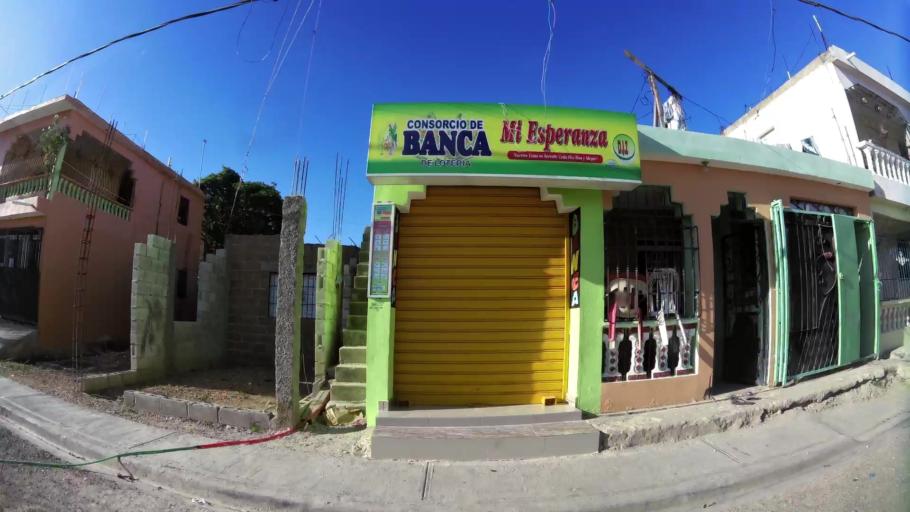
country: DO
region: Santo Domingo
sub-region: Santo Domingo
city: Santo Domingo Este
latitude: 18.4788
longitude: -69.8191
